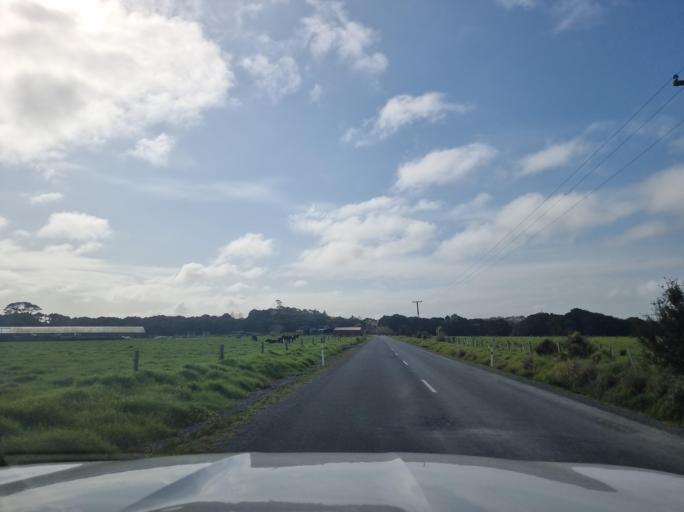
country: NZ
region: Northland
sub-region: Whangarei
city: Ruakaka
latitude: -36.0079
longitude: 174.4533
